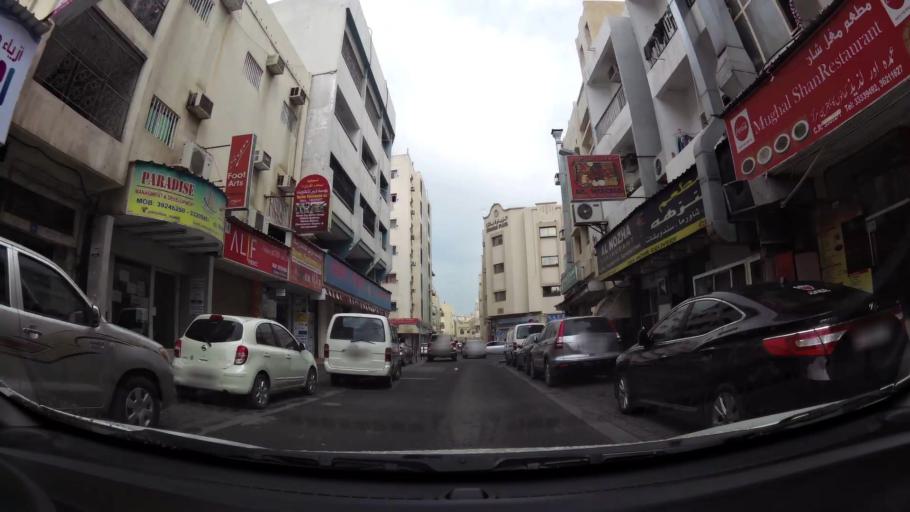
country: BH
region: Manama
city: Manama
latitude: 26.2291
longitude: 50.5918
